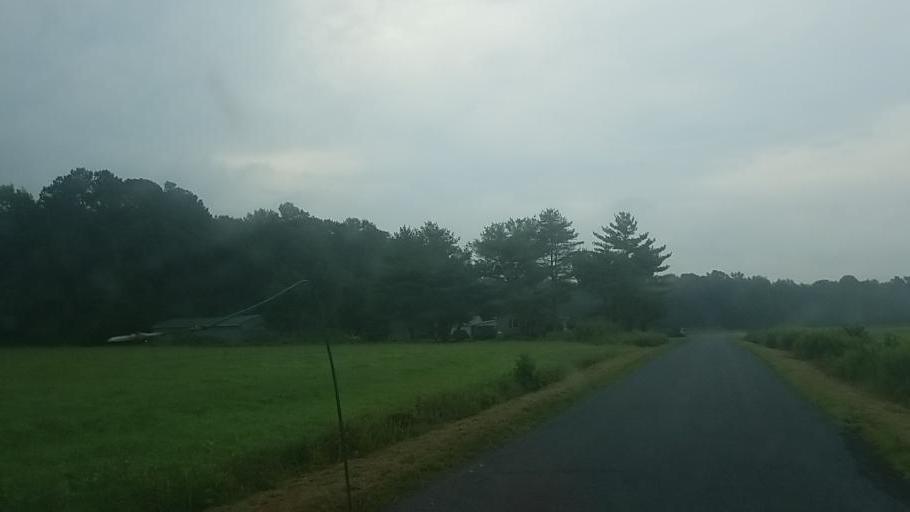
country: US
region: Maryland
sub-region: Wicomico County
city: Pittsville
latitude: 38.4445
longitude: -75.3444
